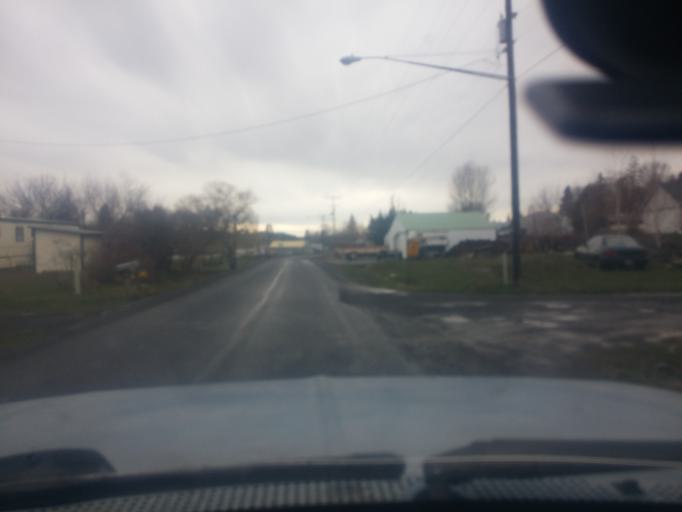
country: US
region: Idaho
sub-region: Latah County
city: Moscow
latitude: 46.9286
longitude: -116.8868
